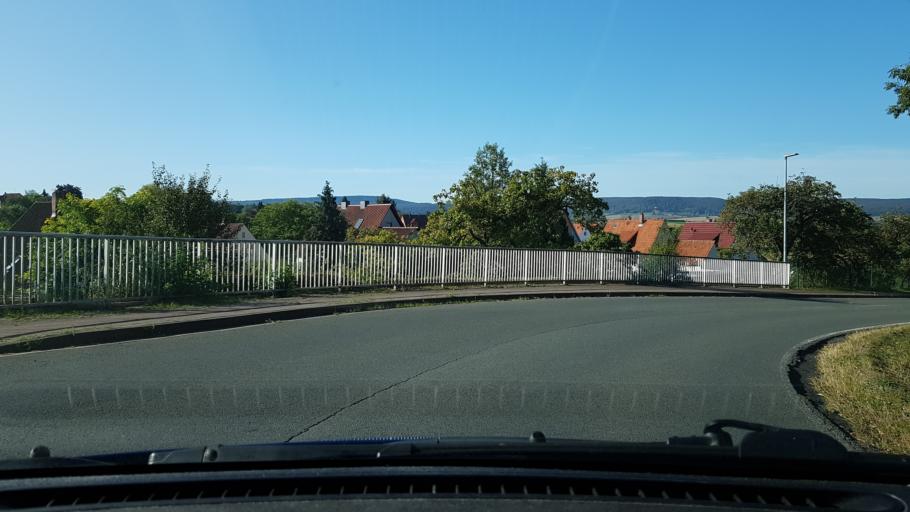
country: DE
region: Lower Saxony
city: Messenkamp
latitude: 52.2387
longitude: 9.4274
